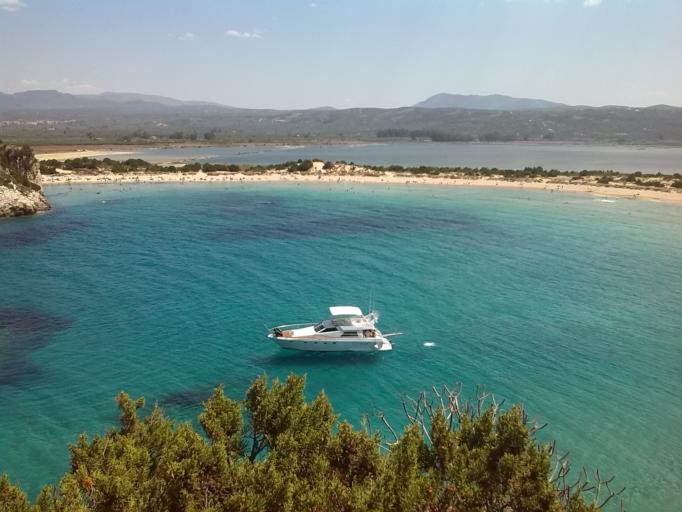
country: GR
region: Peloponnese
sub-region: Nomos Messinias
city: Pylos
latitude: 36.9628
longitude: 21.6592
